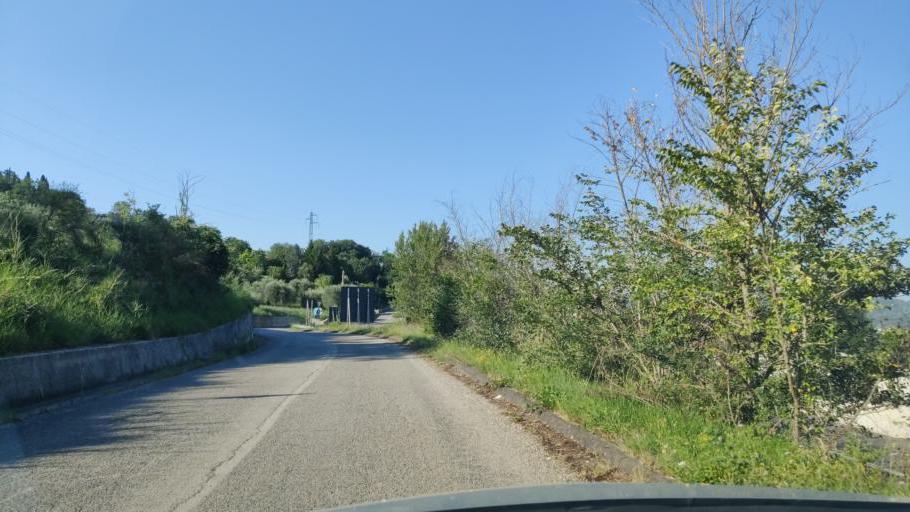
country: IT
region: Latium
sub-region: Provincia di Viterbo
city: Orte Scalo
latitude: 42.4737
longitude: 12.4322
